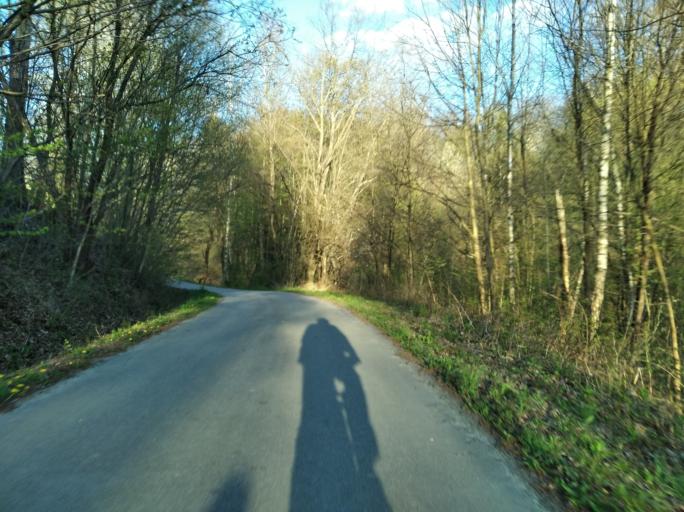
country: PL
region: Subcarpathian Voivodeship
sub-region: Powiat strzyzowski
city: Strzyzow
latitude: 49.8758
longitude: 21.8261
